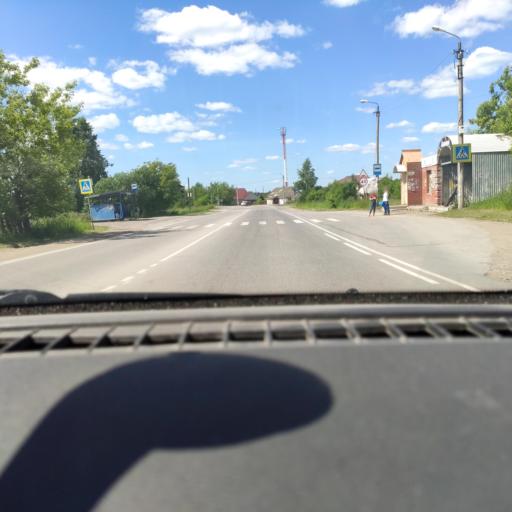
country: RU
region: Perm
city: Ust'-Kachka
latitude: 58.0766
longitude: 55.6724
